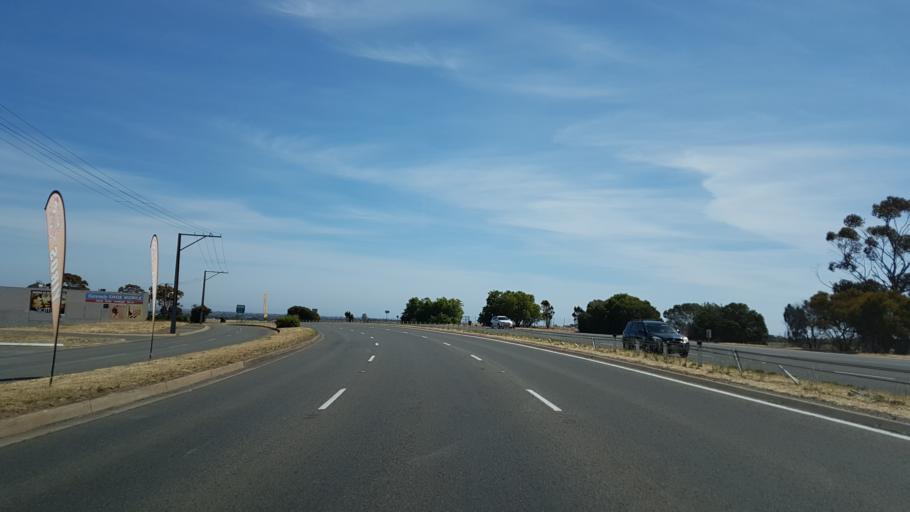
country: AU
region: South Australia
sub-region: Marion
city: Trott Park
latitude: -35.0636
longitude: 138.5557
